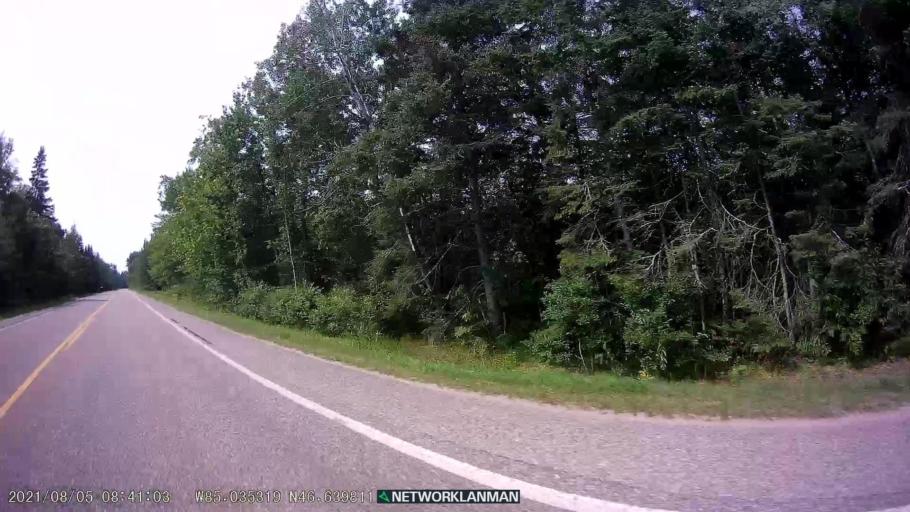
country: US
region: Michigan
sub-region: Luce County
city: Newberry
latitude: 46.6395
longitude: -85.0353
